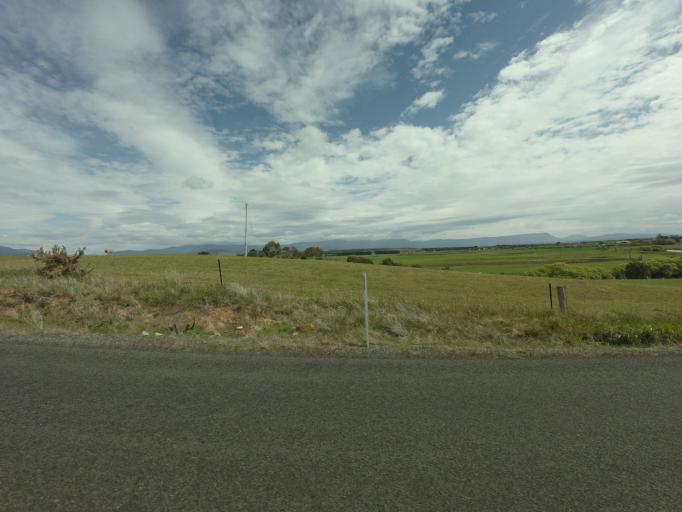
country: AU
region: Tasmania
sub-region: Northern Midlands
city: Longford
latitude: -41.7612
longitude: 147.2092
